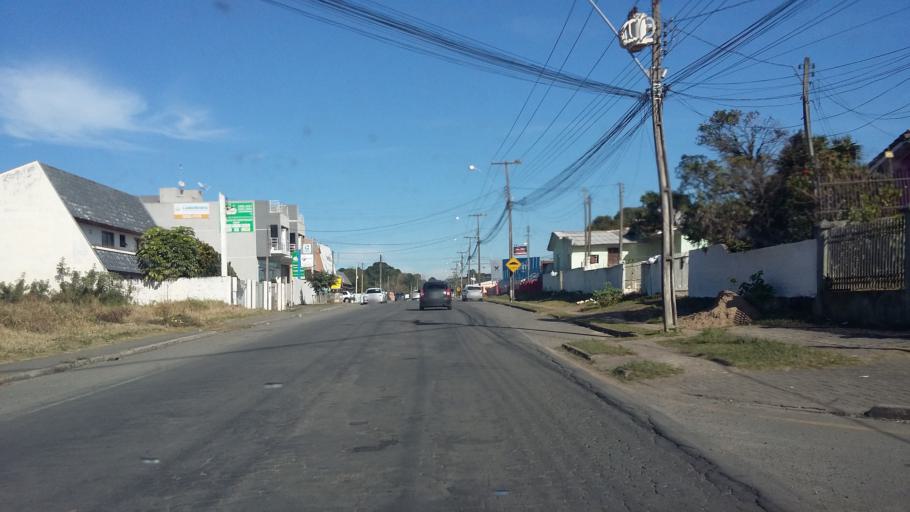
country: BR
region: Parana
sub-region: Campo Largo
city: Campo Largo
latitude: -25.4567
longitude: -49.5428
